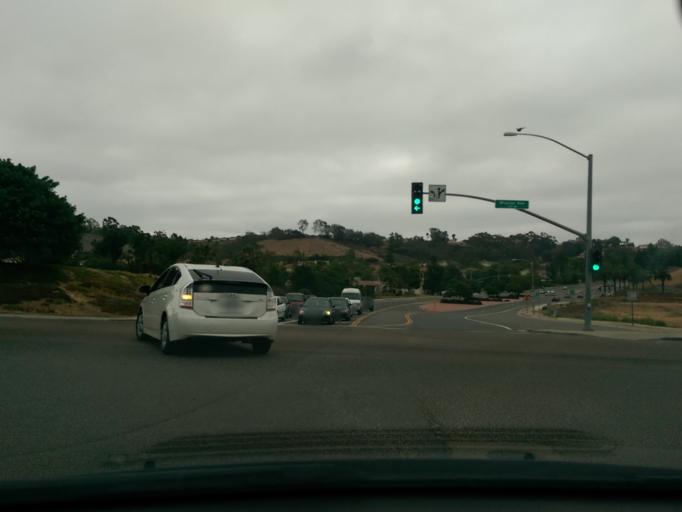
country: US
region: California
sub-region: San Diego County
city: Camp Pendleton South
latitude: 33.2306
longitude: -117.3189
